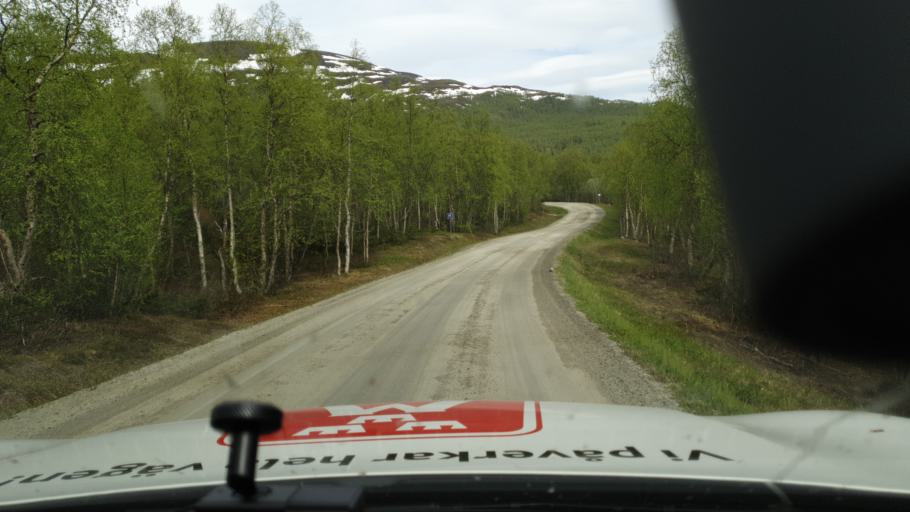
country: NO
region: Nordland
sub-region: Rana
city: Mo i Rana
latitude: 65.7488
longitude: 15.1838
